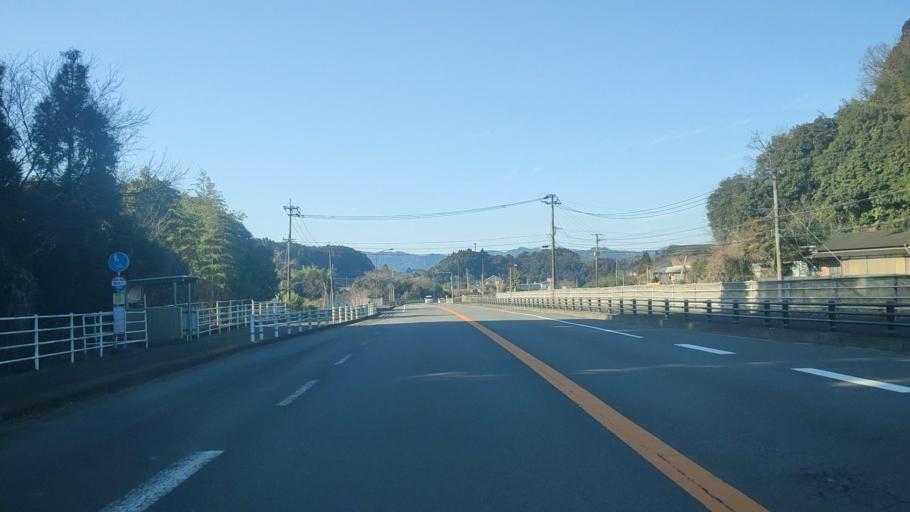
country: JP
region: Oita
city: Usuki
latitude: 33.0568
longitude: 131.6764
